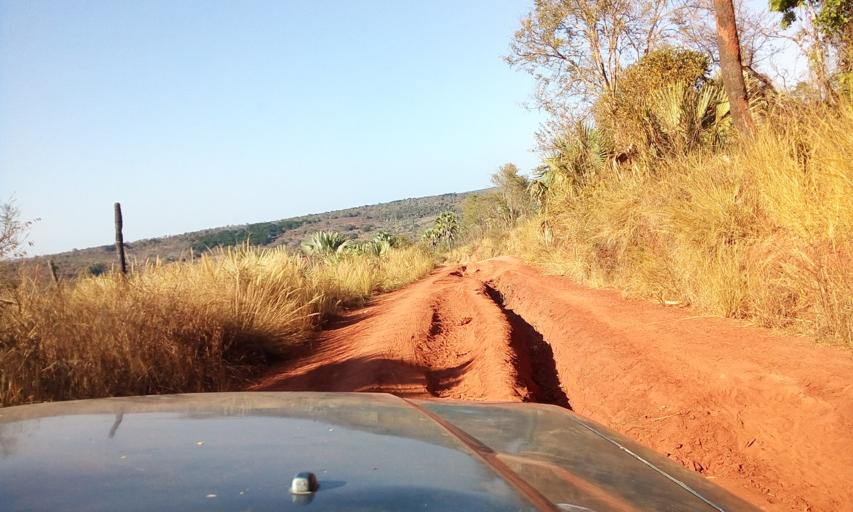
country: MG
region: Melaky
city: Mahabe
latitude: -16.2084
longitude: 45.3533
